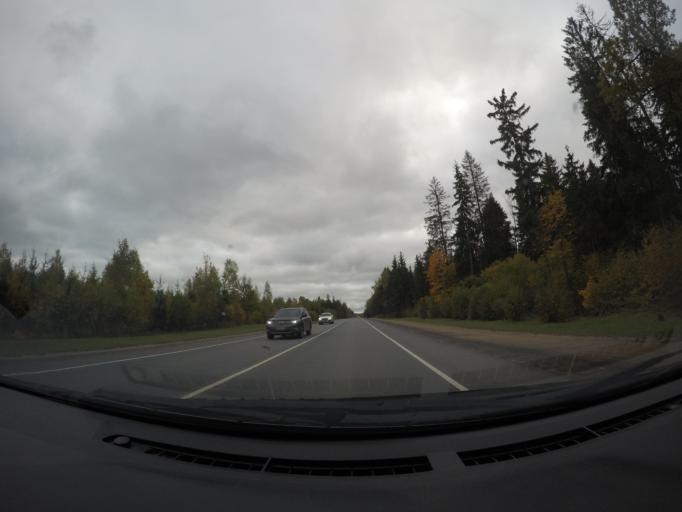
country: RU
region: Moskovskaya
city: Dorokhovo
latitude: 55.6110
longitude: 36.3513
